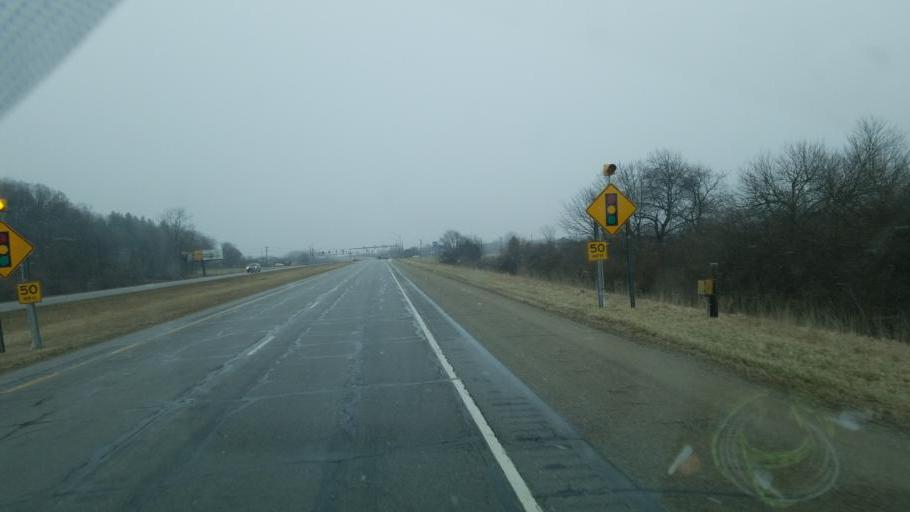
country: US
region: Indiana
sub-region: Miami County
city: Peru
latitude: 40.7730
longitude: -86.0867
